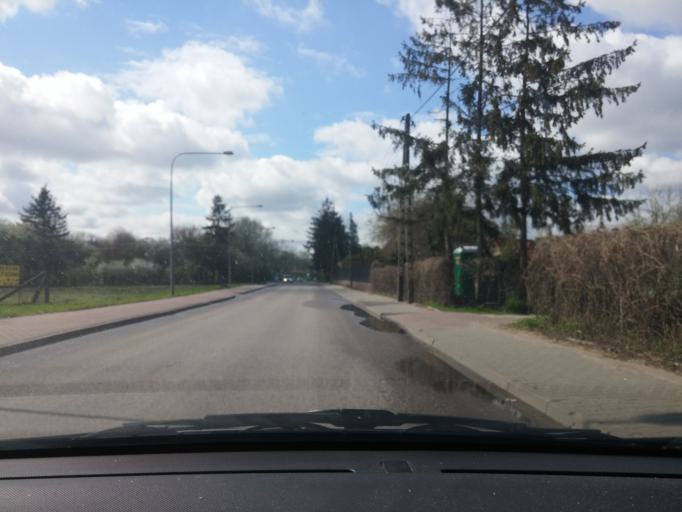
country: PL
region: Masovian Voivodeship
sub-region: Warszawa
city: Wawer
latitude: 52.1845
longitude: 21.1375
